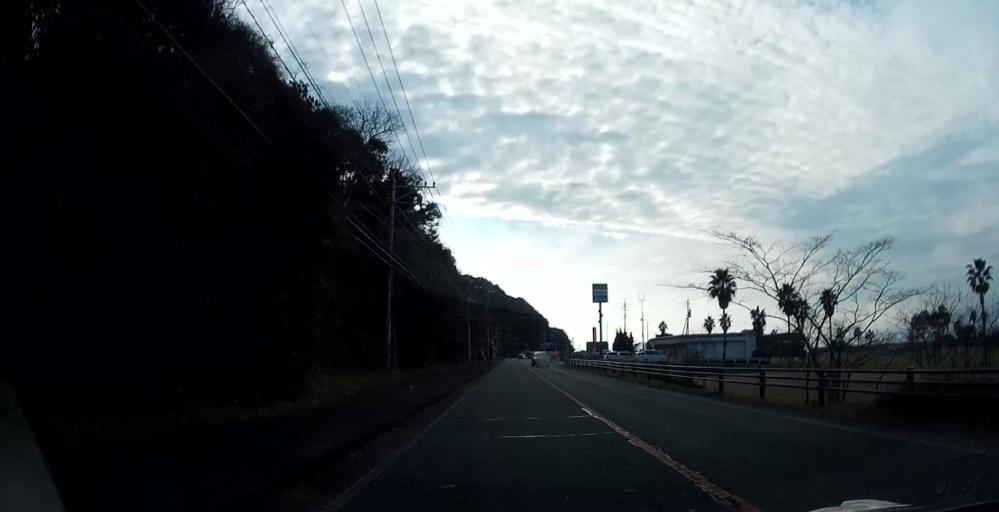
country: JP
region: Kumamoto
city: Matsubase
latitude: 32.6625
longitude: 130.5253
